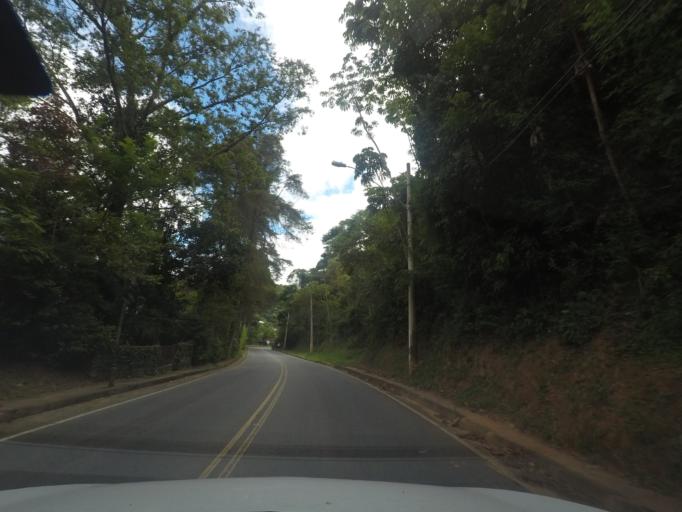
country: BR
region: Rio de Janeiro
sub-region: Teresopolis
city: Teresopolis
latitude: -22.3946
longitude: -42.9891
